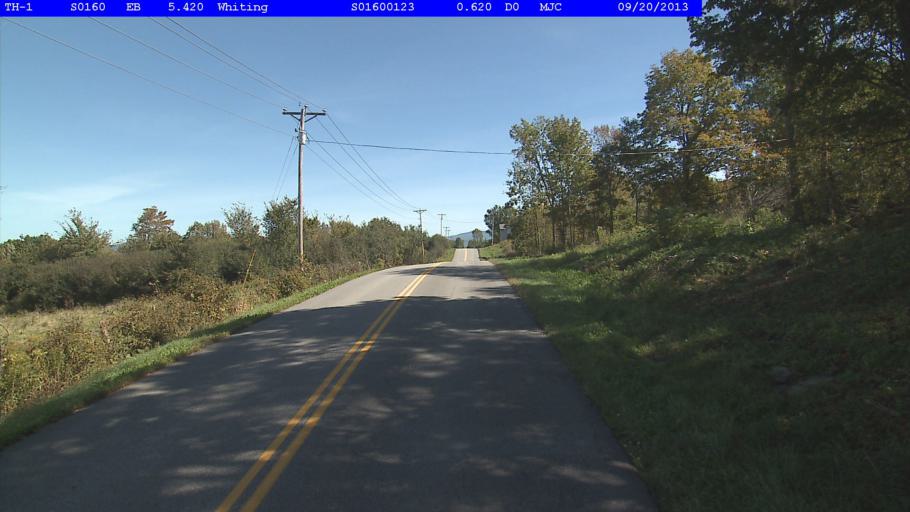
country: US
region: Vermont
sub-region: Rutland County
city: Brandon
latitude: 43.8630
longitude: -73.2132
